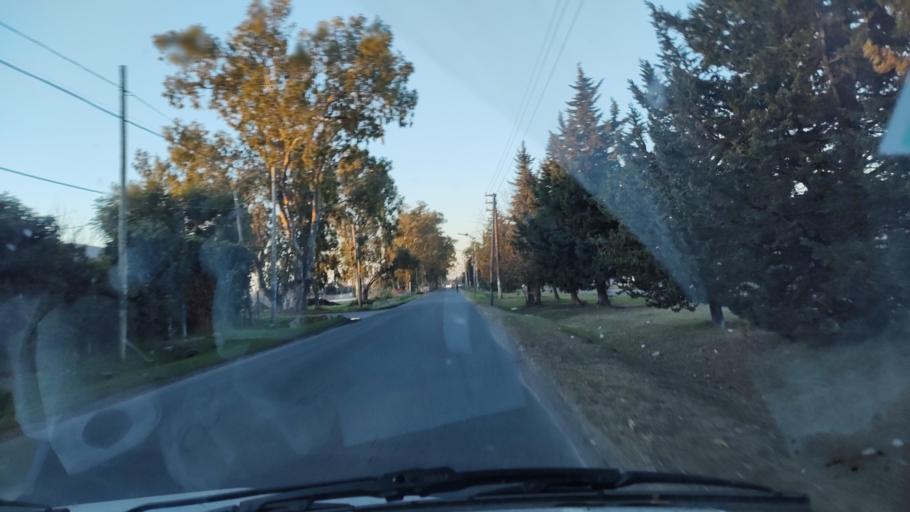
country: AR
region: Buenos Aires
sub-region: Partido de La Plata
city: La Plata
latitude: -34.9051
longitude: -58.0324
